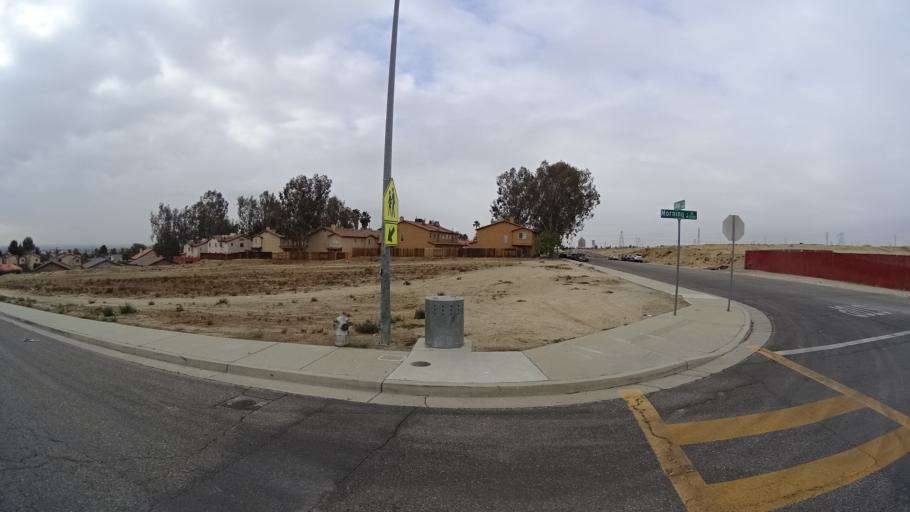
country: US
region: California
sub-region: Kern County
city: Bakersfield
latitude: 35.3835
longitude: -118.9142
